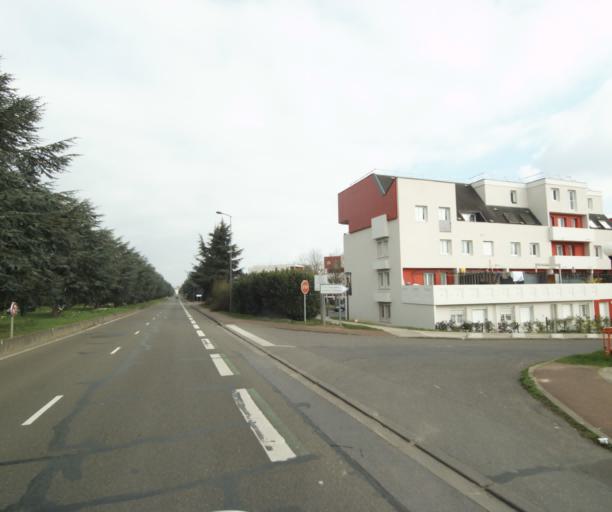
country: FR
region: Ile-de-France
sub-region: Departement du Val-d'Oise
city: Osny
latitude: 49.0479
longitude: 2.0479
